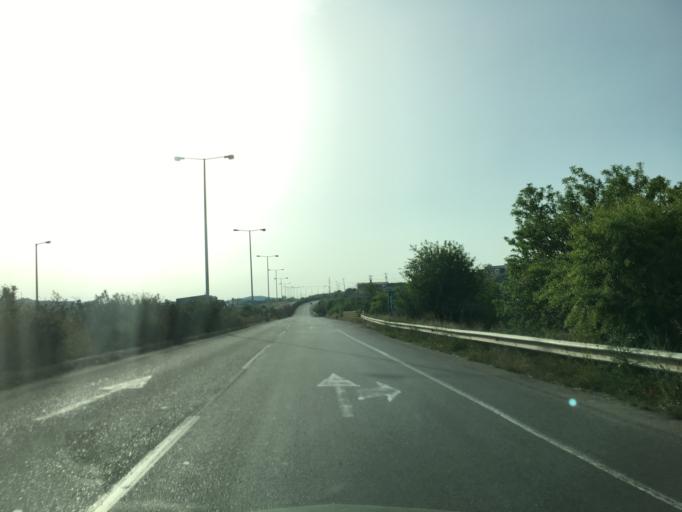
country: GR
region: Thessaly
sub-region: Nomos Magnisias
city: Nea Ionia
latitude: 39.3777
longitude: 22.8833
